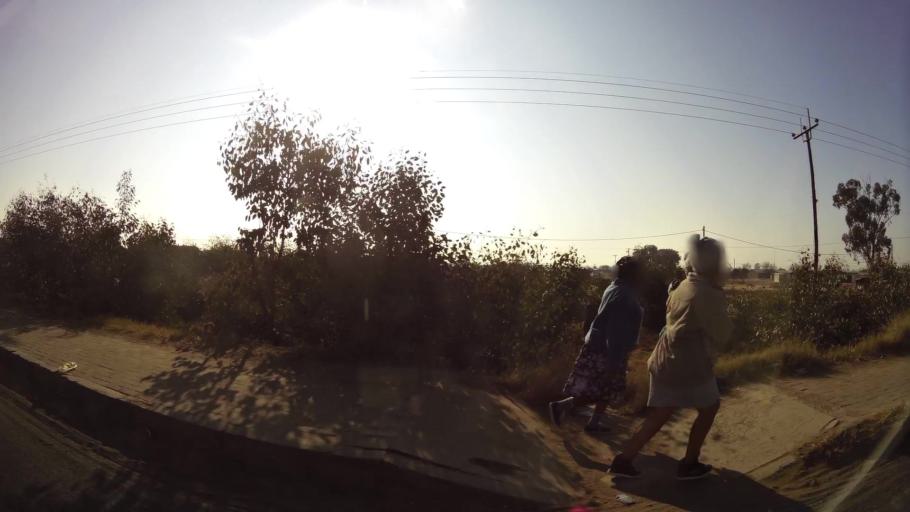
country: ZA
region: Orange Free State
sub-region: Mangaung Metropolitan Municipality
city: Bloemfontein
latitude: -29.1685
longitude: 26.2604
